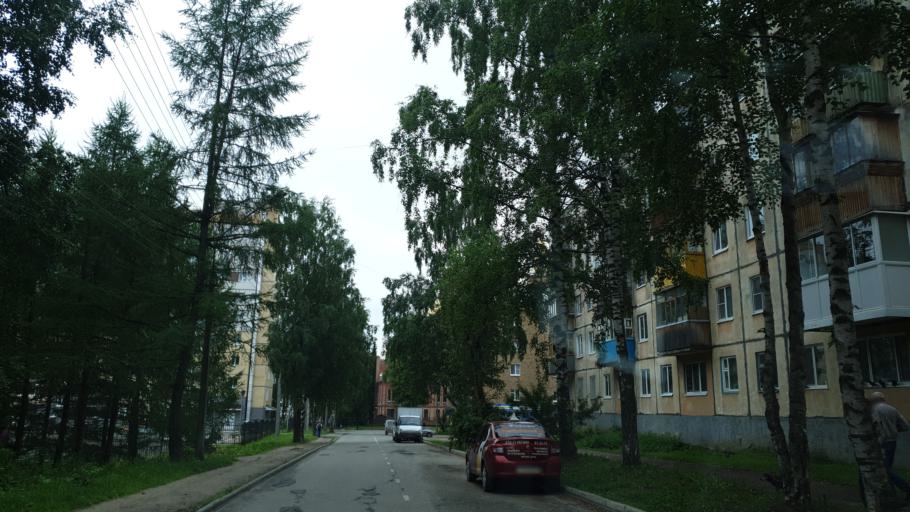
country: RU
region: Komi Republic
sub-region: Syktyvdinskiy Rayon
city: Syktyvkar
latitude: 61.6609
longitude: 50.8235
